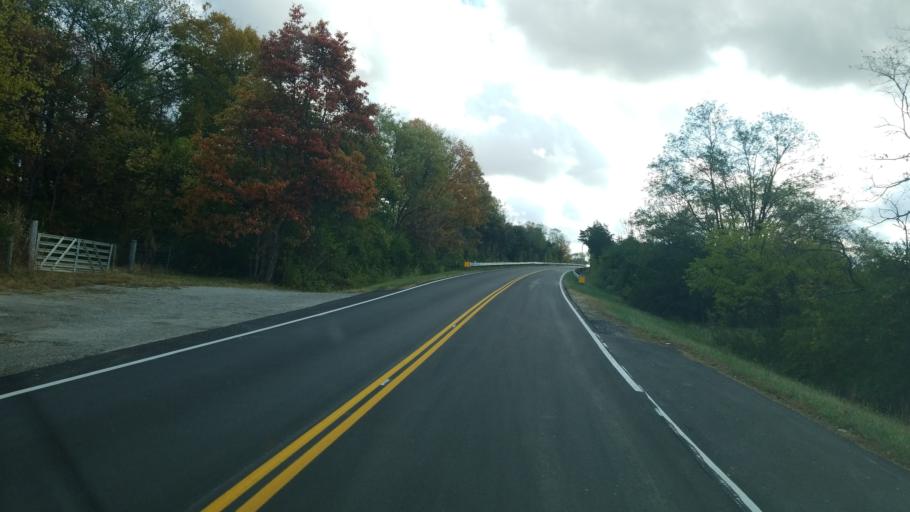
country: US
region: Ohio
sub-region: Warren County
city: Morrow
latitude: 39.4300
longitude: -84.0834
